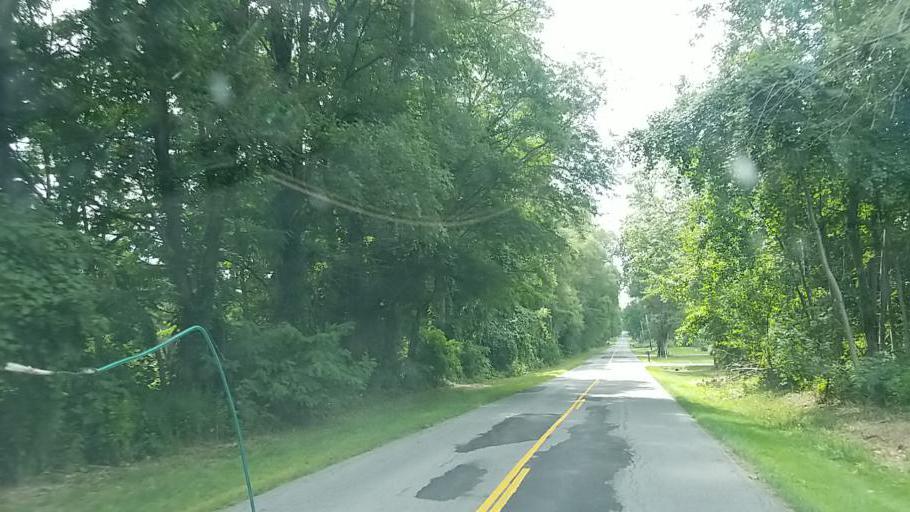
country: US
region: Michigan
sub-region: Kent County
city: Walker
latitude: 43.0359
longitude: -85.7388
